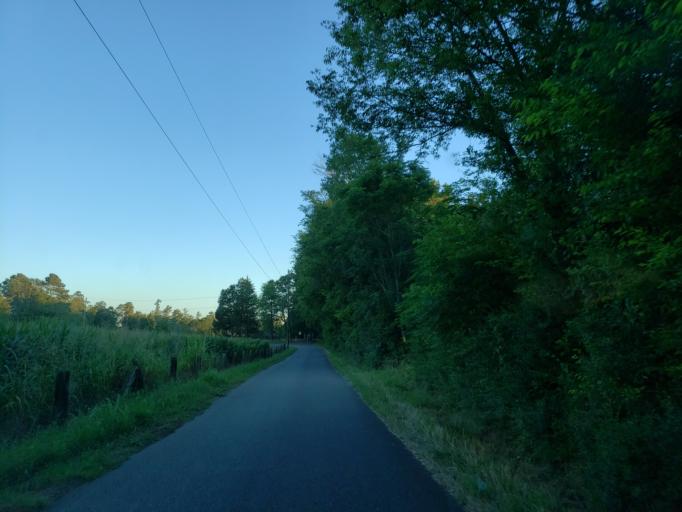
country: US
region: Georgia
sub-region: Bartow County
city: Euharlee
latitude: 34.1106
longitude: -84.8826
